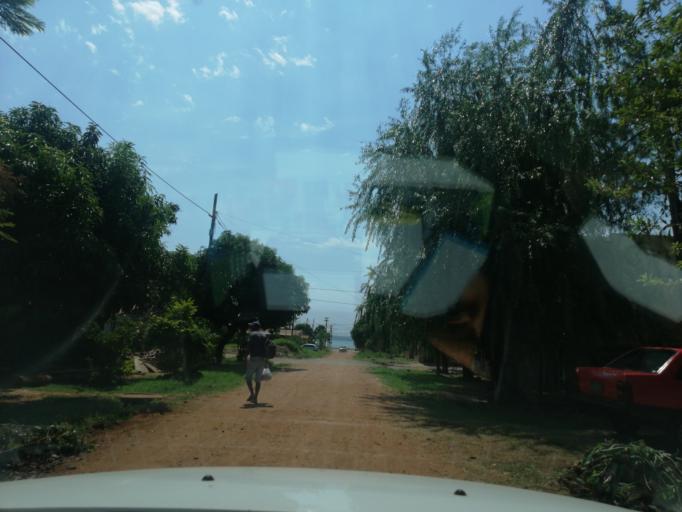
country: AR
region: Misiones
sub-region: Departamento de Capital
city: Posadas
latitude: -27.4269
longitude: -55.8760
